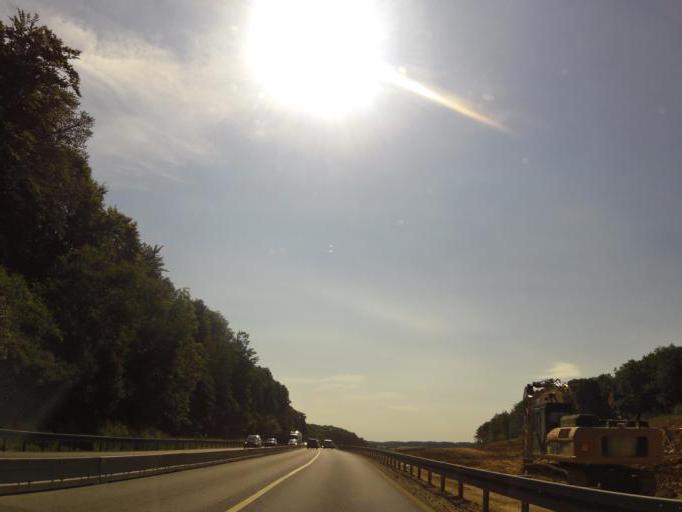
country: DE
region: Baden-Wuerttemberg
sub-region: Tuebingen Region
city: Nellingen
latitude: 48.5160
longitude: 9.8224
